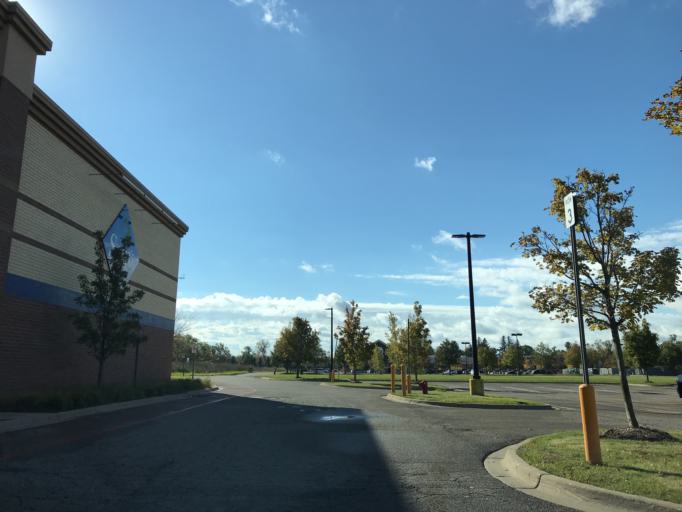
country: US
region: Michigan
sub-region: Oakland County
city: Wixom
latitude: 42.4909
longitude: -83.5336
